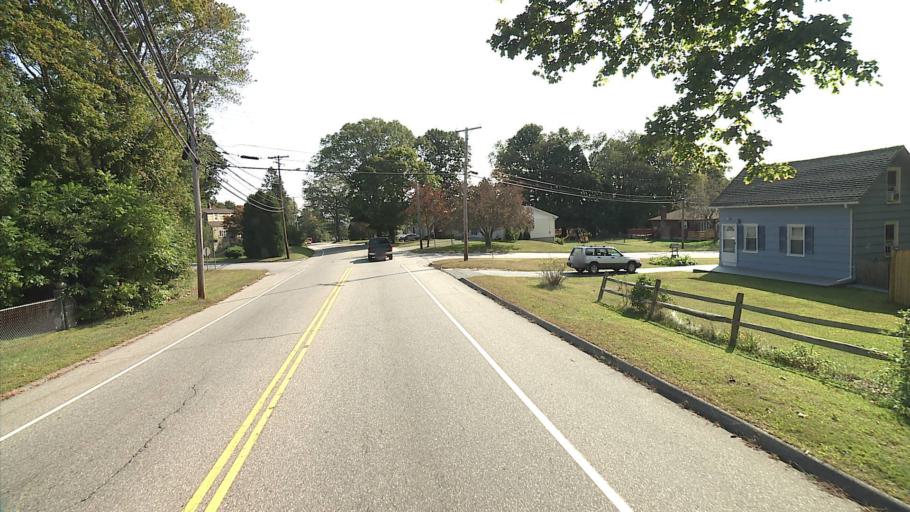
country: US
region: Connecticut
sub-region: New London County
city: Norwich
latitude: 41.5576
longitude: -72.0747
